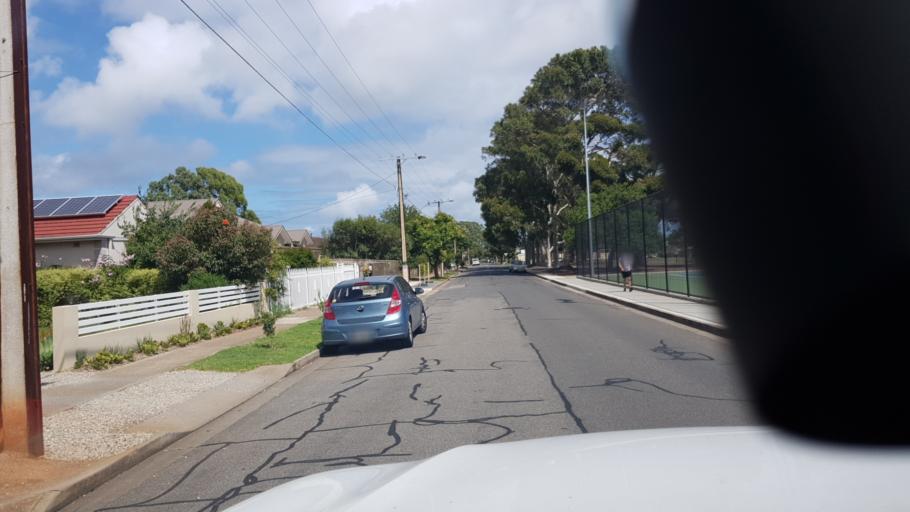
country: AU
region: South Australia
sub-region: Marion
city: Sturt
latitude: -35.0167
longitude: 138.5376
